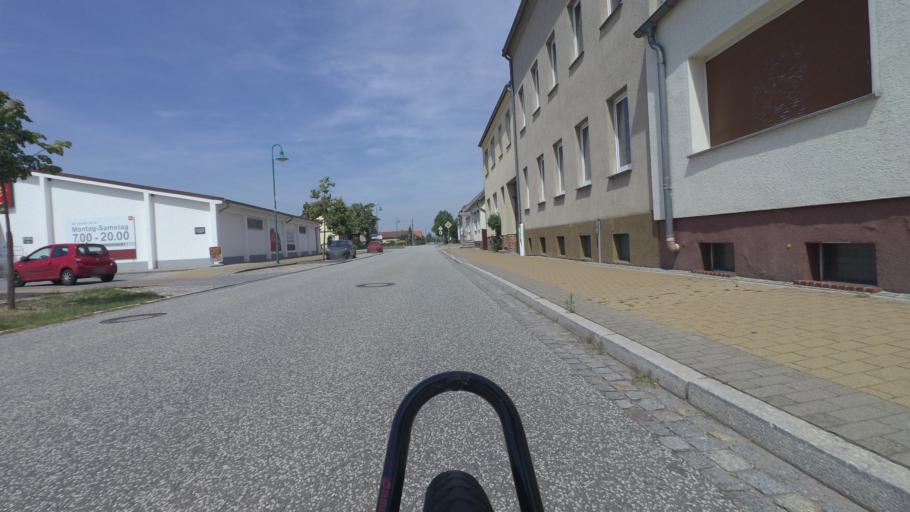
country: DE
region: Brandenburg
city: Rhinow
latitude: 52.7520
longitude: 12.3406
